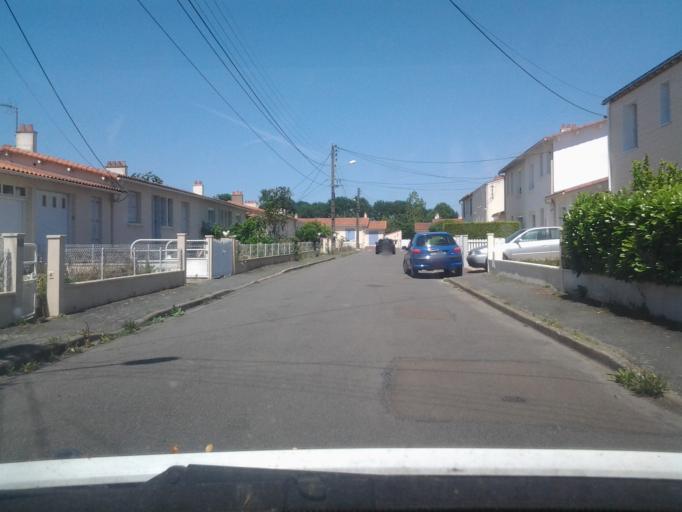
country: FR
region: Pays de la Loire
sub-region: Departement de la Vendee
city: La Roche-sur-Yon
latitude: 46.6643
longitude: -1.4067
